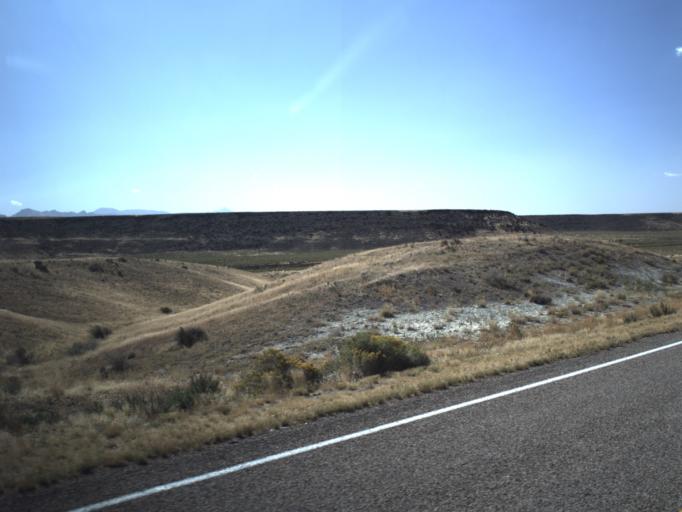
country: US
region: Utah
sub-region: Beaver County
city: Milford
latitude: 38.7677
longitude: -112.9364
